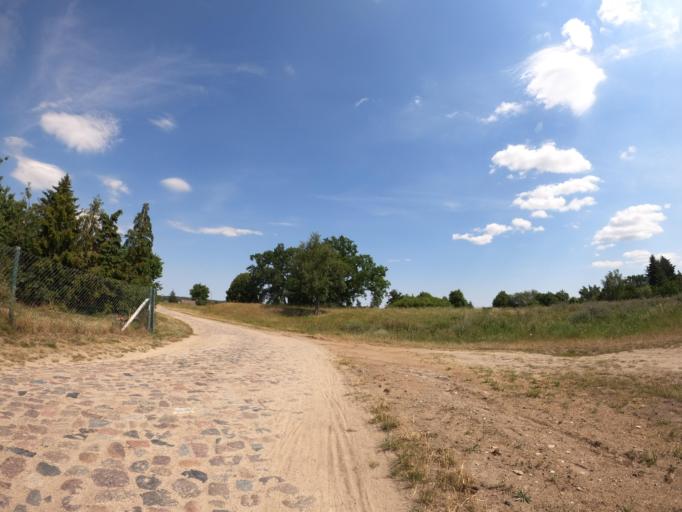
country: DE
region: Brandenburg
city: Mittenwalde
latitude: 53.2968
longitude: 13.5652
